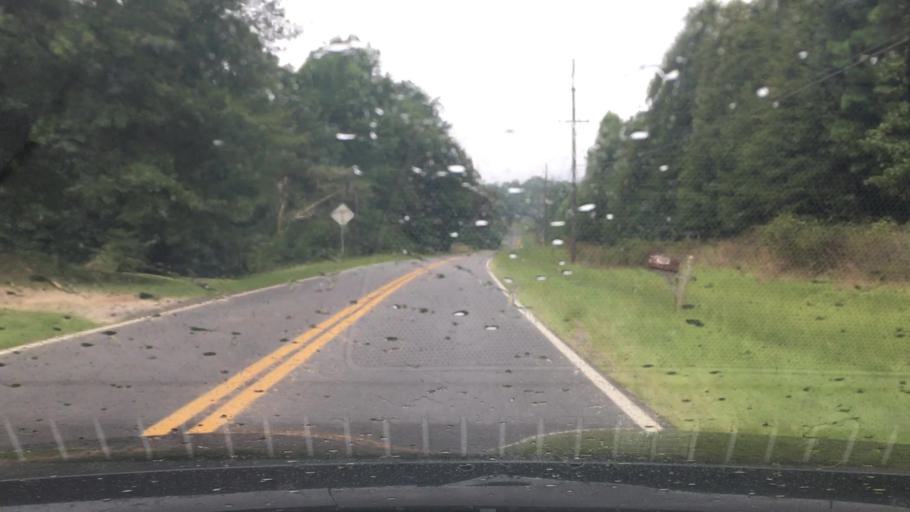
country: US
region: Georgia
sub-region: Spalding County
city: Experiment
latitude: 33.2627
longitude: -84.3872
